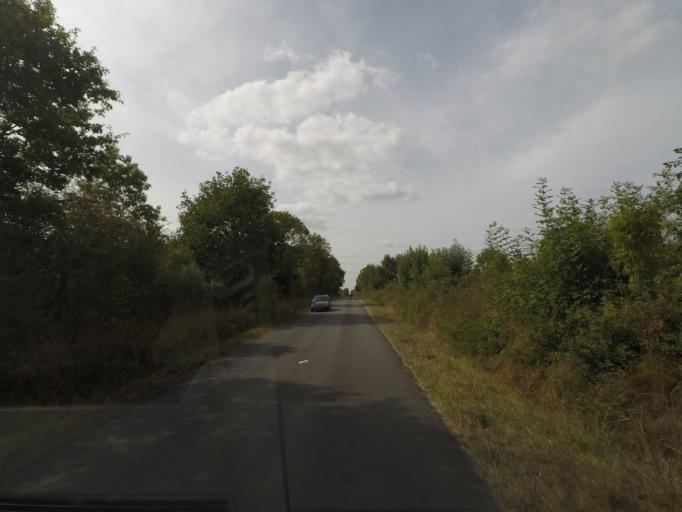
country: FR
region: Poitou-Charentes
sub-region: Departement de la Charente
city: Loubert
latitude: 45.9375
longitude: 0.5341
